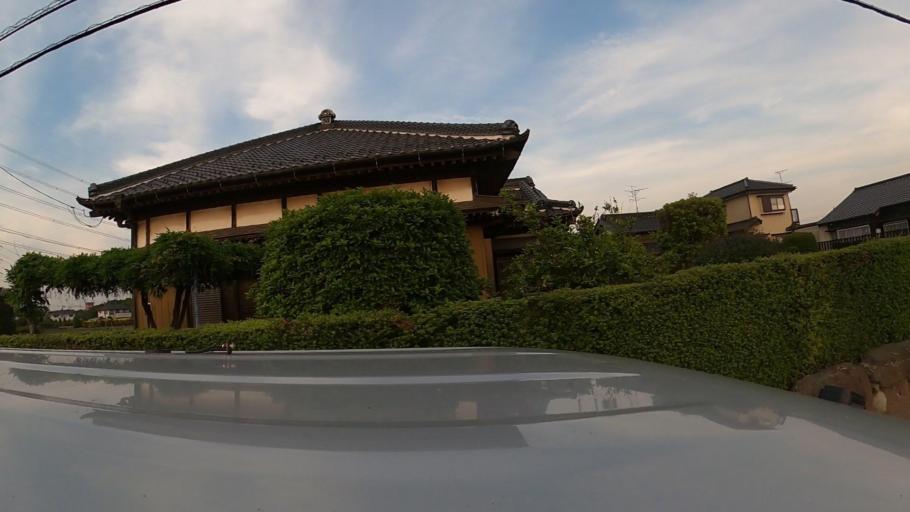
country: JP
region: Ibaraki
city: Ushiku
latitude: 36.0013
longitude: 140.1243
